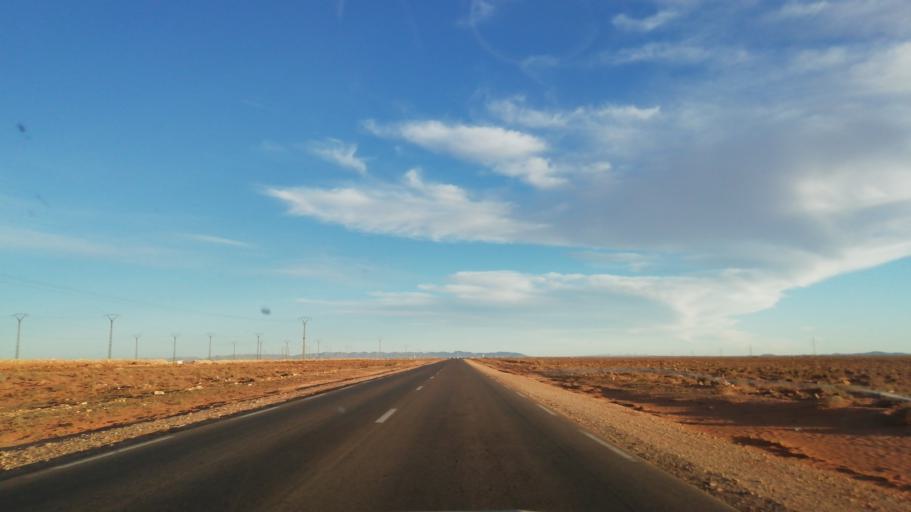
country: DZ
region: Wilaya de Naama
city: Naama
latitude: 33.7372
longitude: -0.7656
